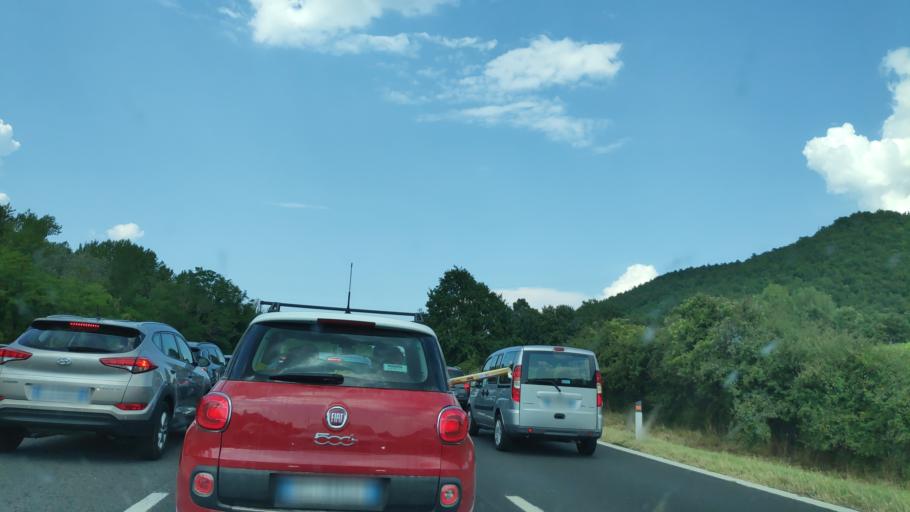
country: IT
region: Umbria
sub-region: Provincia di Terni
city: Stazione di Allerona
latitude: 42.8084
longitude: 12.0356
